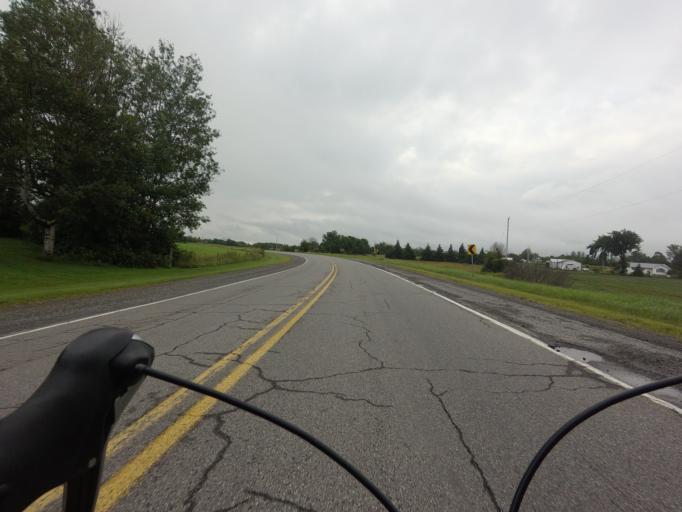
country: CA
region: Ontario
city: Bells Corners
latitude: 45.1617
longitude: -75.8026
